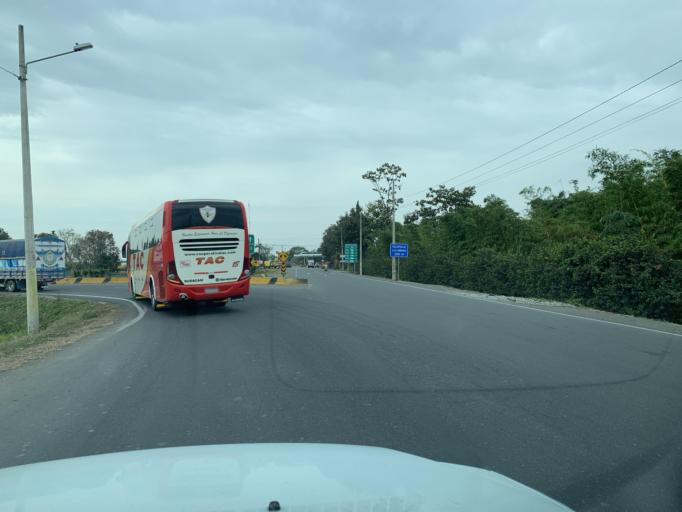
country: EC
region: Guayas
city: Yaguachi Nuevo
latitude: -2.2352
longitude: -79.6393
